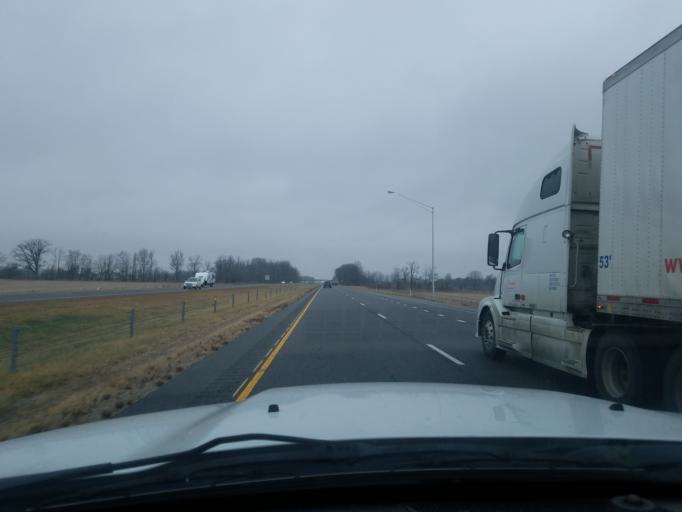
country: US
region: Indiana
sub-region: Madison County
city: Alexandria
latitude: 40.2816
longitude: -85.5580
